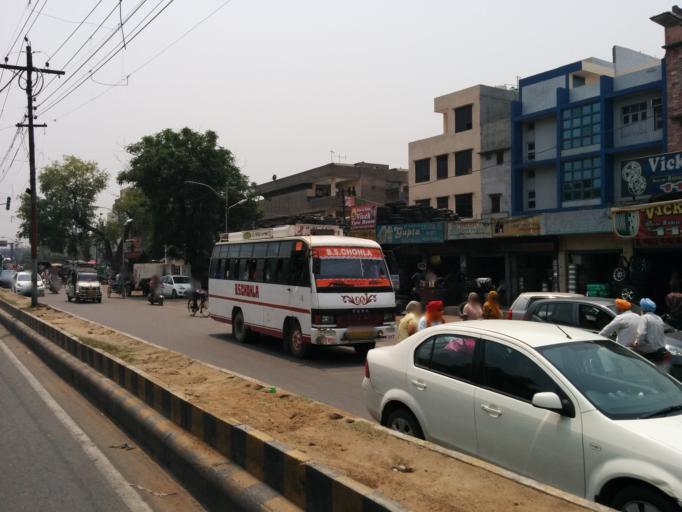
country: IN
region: Punjab
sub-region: Amritsar
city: Amritsar
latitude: 31.6283
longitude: 74.8823
